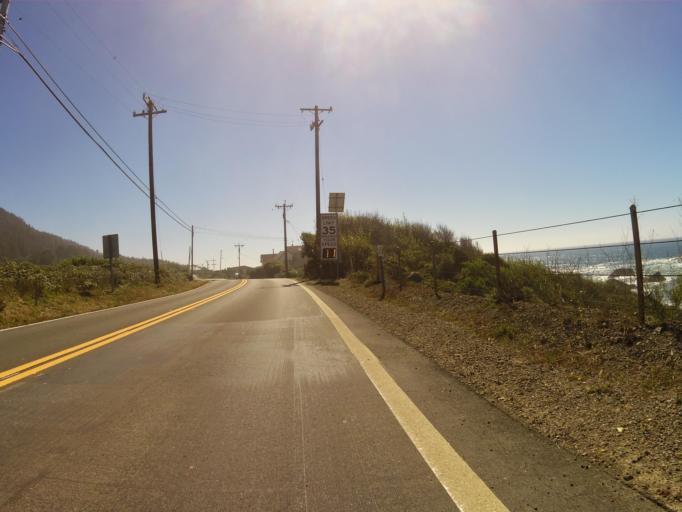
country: US
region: California
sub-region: Mendocino County
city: Fort Bragg
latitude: 39.6408
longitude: -123.7848
